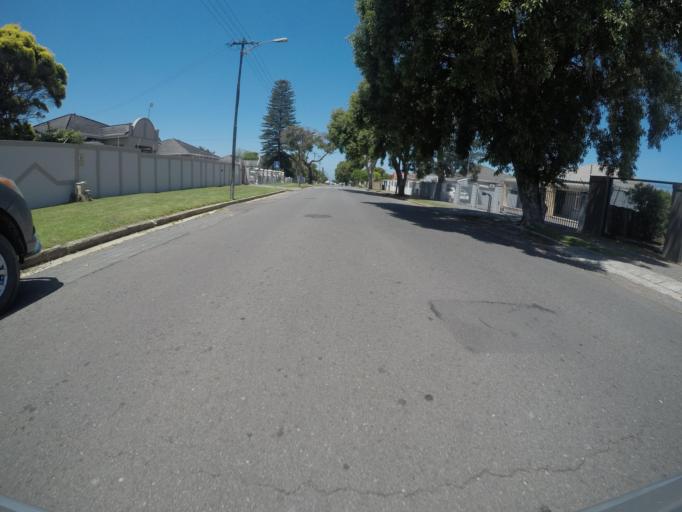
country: ZA
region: Eastern Cape
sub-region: Buffalo City Metropolitan Municipality
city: East London
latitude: -32.9896
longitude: 27.9079
